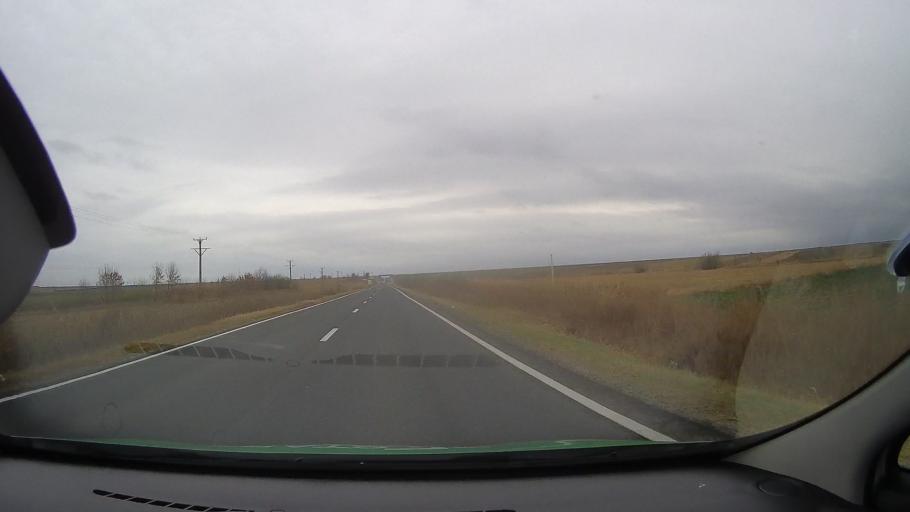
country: RO
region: Constanta
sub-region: Comuna Nicolae Balcescu
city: Nicolae Balcescu
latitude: 44.3846
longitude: 28.3948
